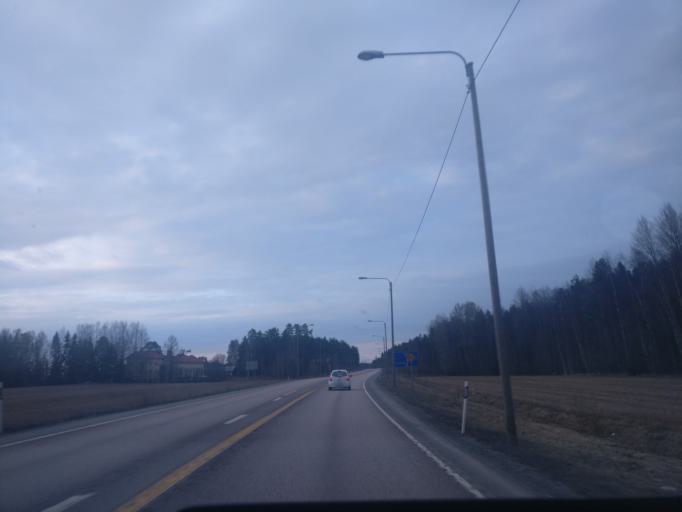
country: FI
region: Paijanne Tavastia
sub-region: Lahti
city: Hartola
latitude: 61.5015
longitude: 25.9812
